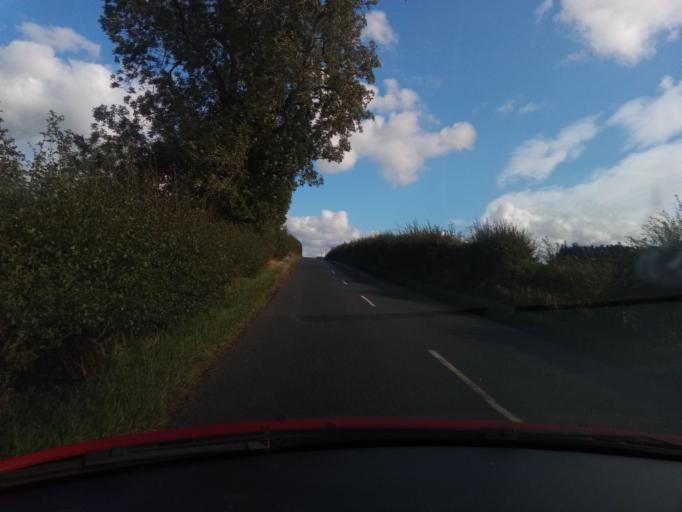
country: GB
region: Scotland
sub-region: The Scottish Borders
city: Kelso
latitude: 55.5707
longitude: -2.3699
